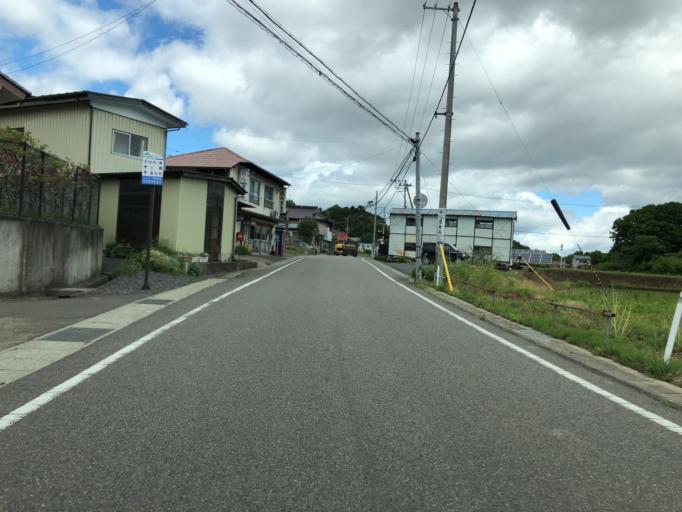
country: JP
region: Fukushima
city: Miharu
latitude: 37.4729
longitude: 140.4592
